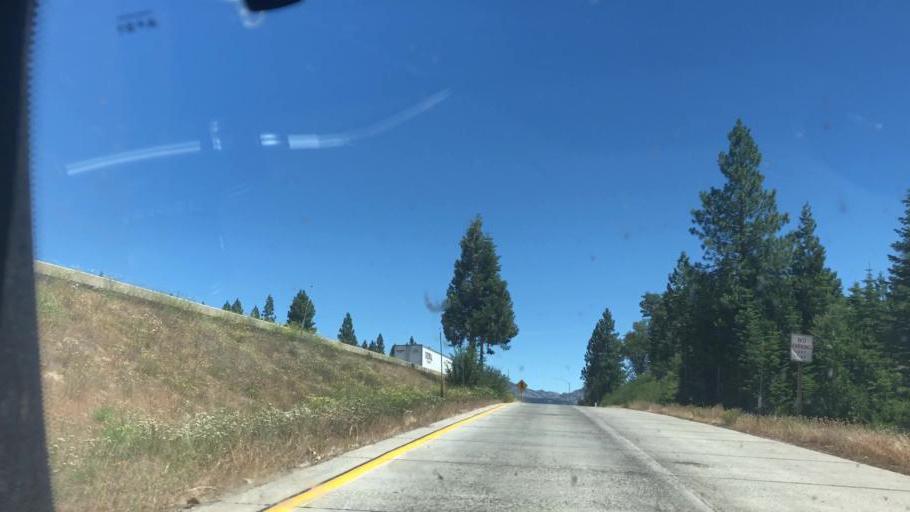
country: US
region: California
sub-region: Sierra County
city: Downieville
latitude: 39.2926
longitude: -120.6784
